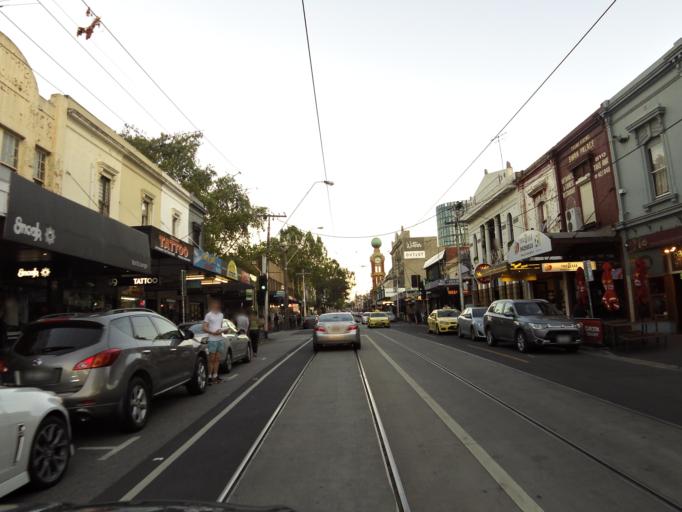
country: AU
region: Victoria
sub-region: Melbourne
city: East Melbourne
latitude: -37.8251
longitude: 144.9929
